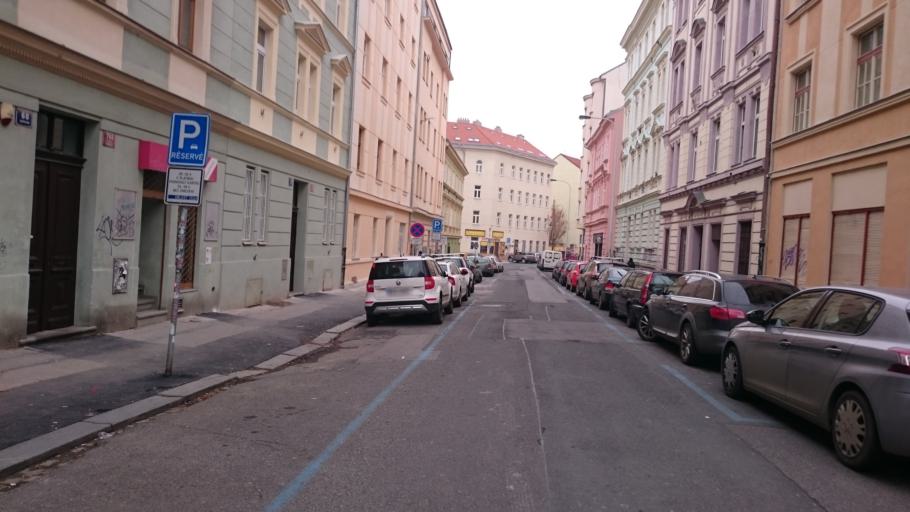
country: CZ
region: Praha
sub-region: Praha 8
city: Karlin
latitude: 50.0833
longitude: 14.4505
